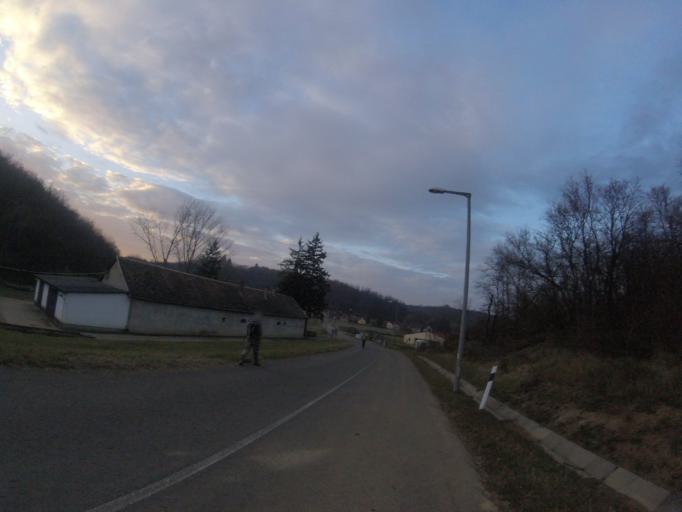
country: HU
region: Tolna
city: Bonyhad
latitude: 46.2229
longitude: 18.6090
